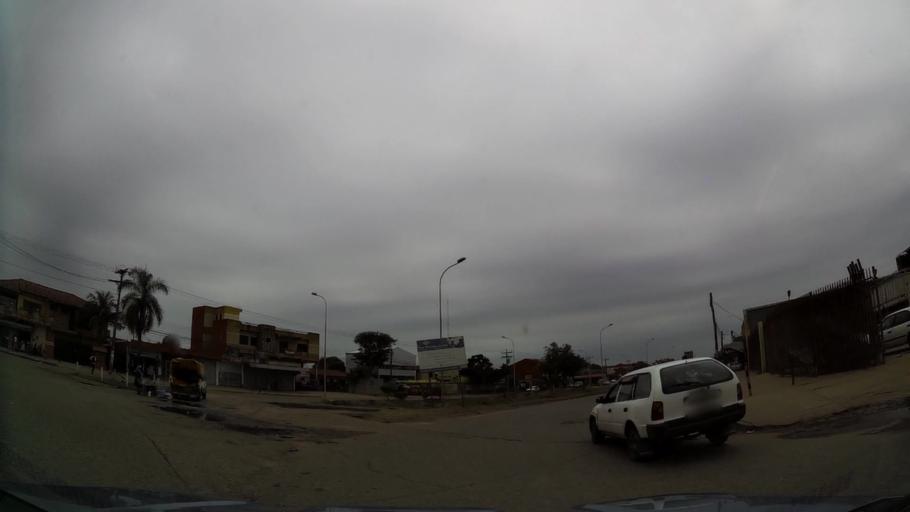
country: BO
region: Santa Cruz
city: Santa Cruz de la Sierra
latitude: -17.8314
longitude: -63.1756
